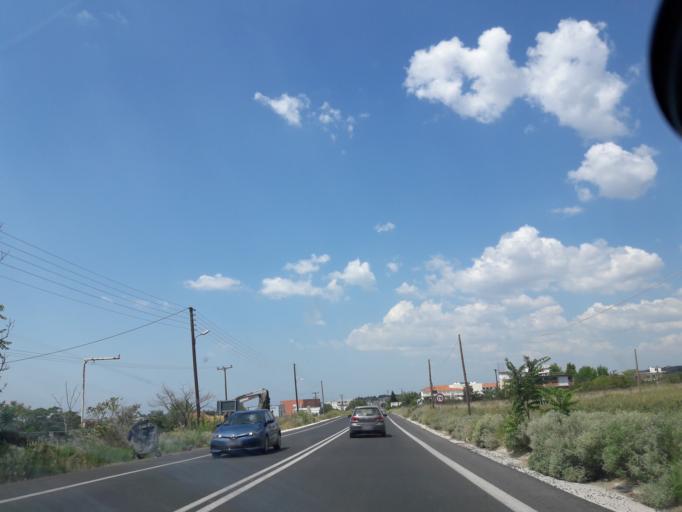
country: GR
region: Central Macedonia
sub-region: Nomos Thessalonikis
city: Agia Paraskevi
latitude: 40.5140
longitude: 23.0740
